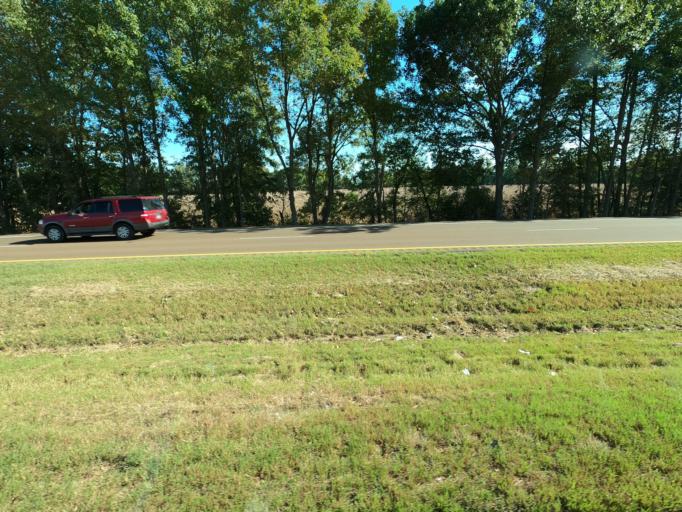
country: US
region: Tennessee
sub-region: Obion County
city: Englewood
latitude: 36.3651
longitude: -89.1289
